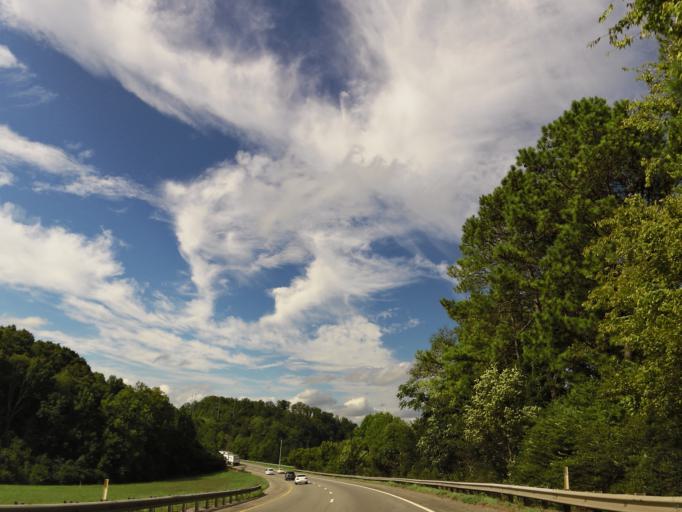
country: US
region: Tennessee
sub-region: Loudon County
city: Lenoir City
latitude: 35.8687
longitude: -84.2573
